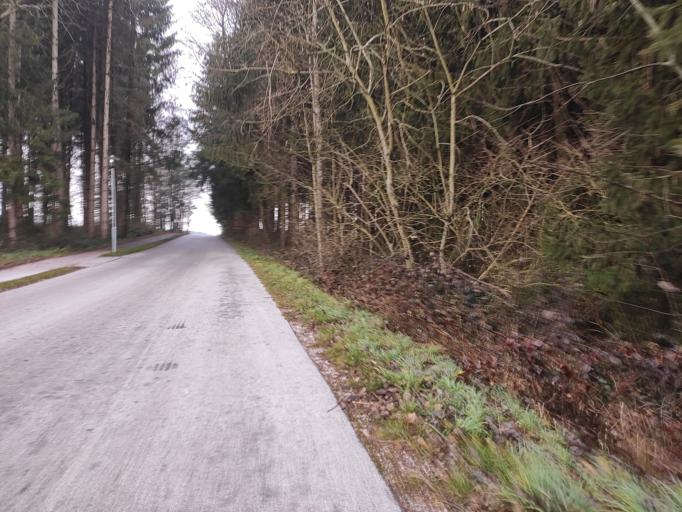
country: AT
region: Salzburg
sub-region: Politischer Bezirk Salzburg-Umgebung
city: Berndorf bei Salzburg
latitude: 48.0035
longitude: 13.0893
